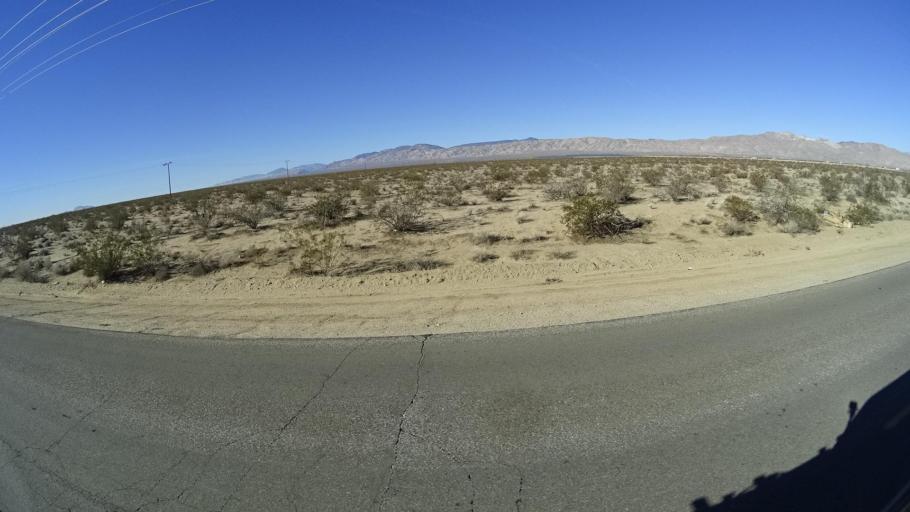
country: US
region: California
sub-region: Kern County
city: California City
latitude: 35.1847
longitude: -117.9854
